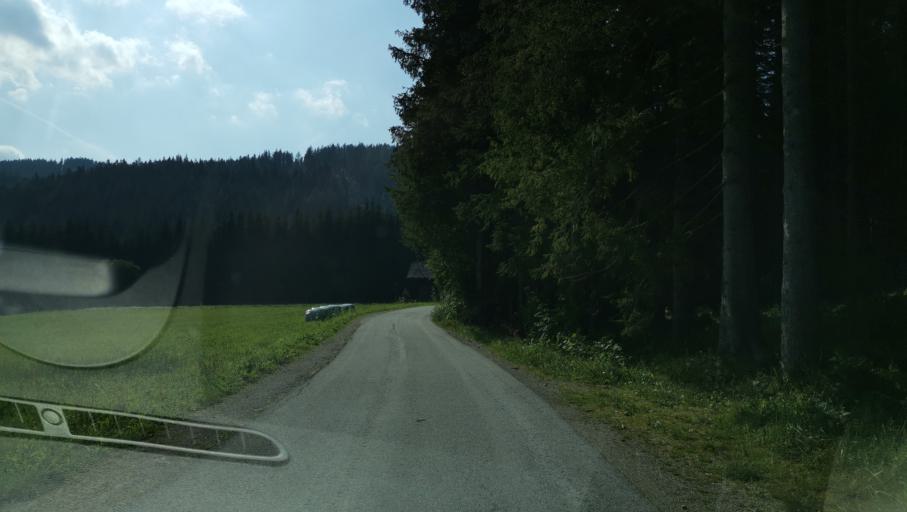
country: AT
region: Styria
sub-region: Politischer Bezirk Liezen
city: Trieben
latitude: 47.5270
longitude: 14.4686
